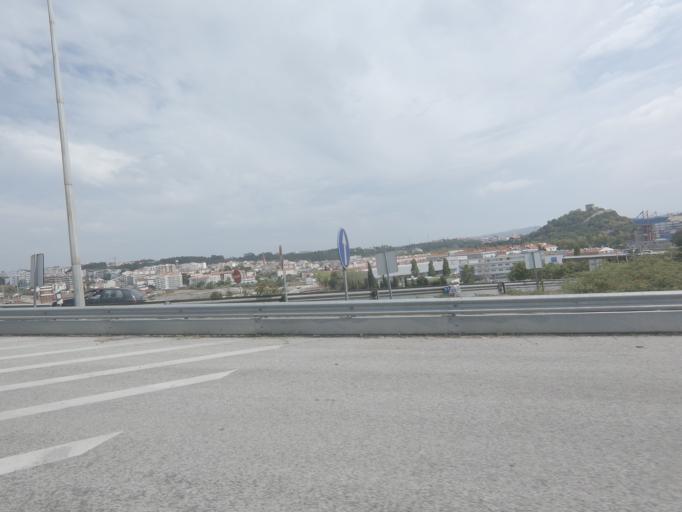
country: PT
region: Leiria
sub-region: Leiria
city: Leiria
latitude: 39.7556
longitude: -8.8148
